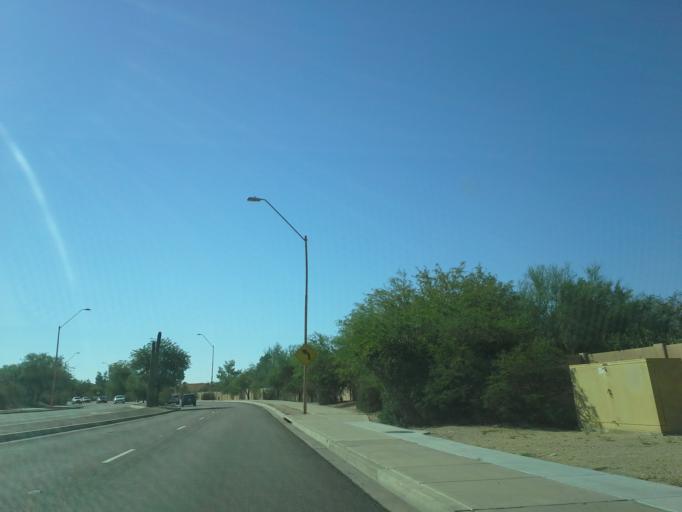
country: US
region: Arizona
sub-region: Maricopa County
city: Scottsdale
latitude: 33.6045
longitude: -111.8549
